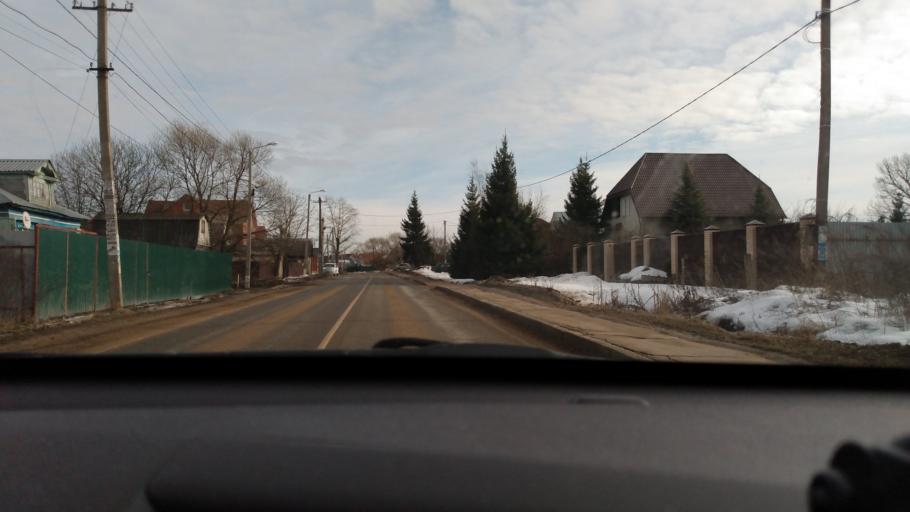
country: RU
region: Moskovskaya
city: Nakhabino
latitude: 55.8918
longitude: 37.1740
